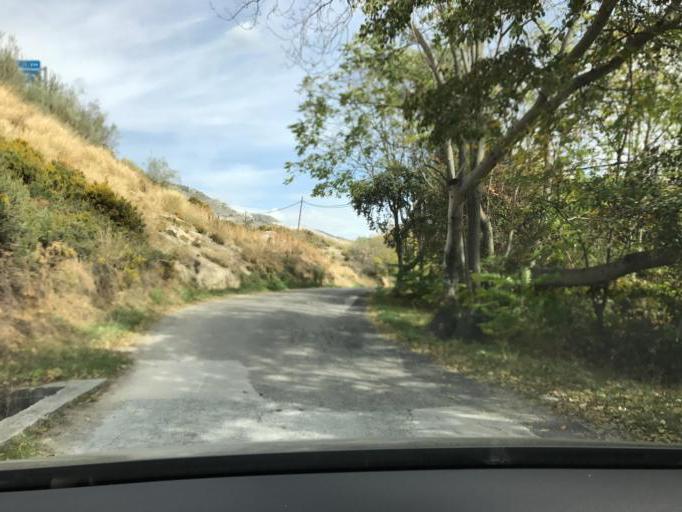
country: ES
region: Andalusia
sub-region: Provincia de Granada
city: Huetor Santillan
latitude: 37.2272
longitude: -3.5051
